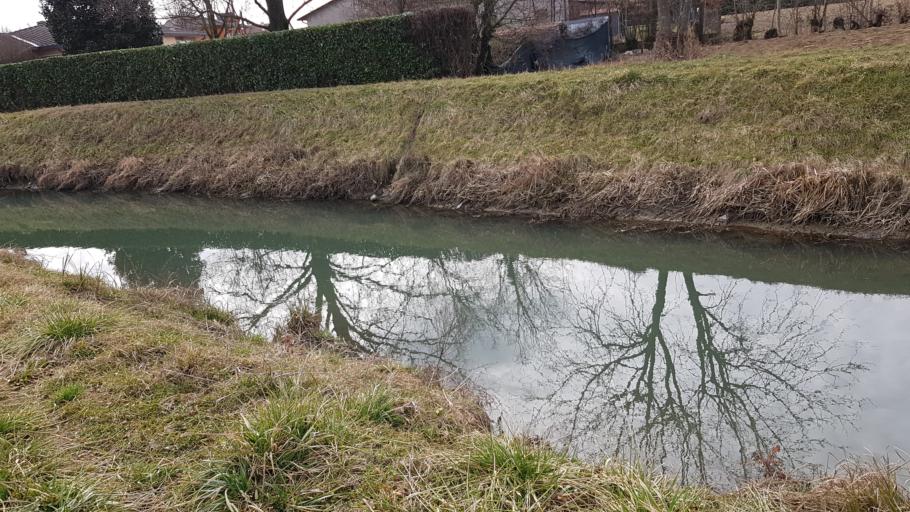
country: IT
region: Veneto
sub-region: Provincia di Padova
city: San Giorgio delle Pertiche
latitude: 45.5447
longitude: 11.9086
